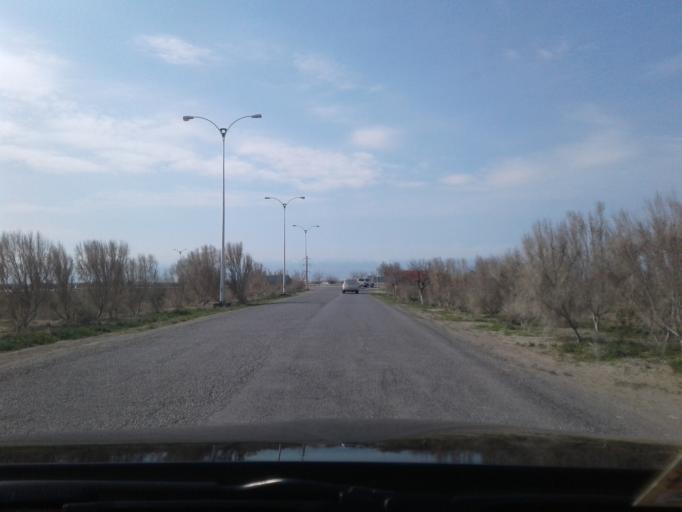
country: TM
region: Ahal
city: Ashgabat
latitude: 38.0909
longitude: 58.3819
